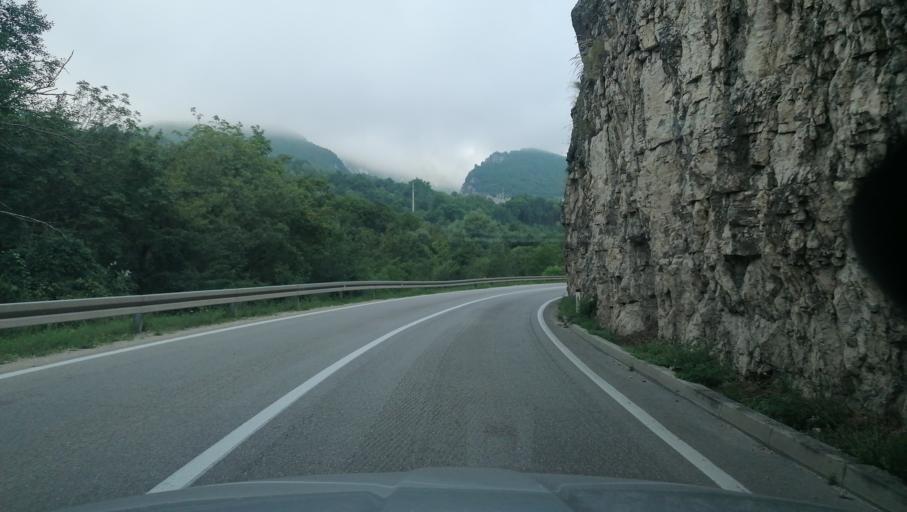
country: BA
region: Federation of Bosnia and Herzegovina
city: Divicani
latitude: 44.3720
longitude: 17.2958
